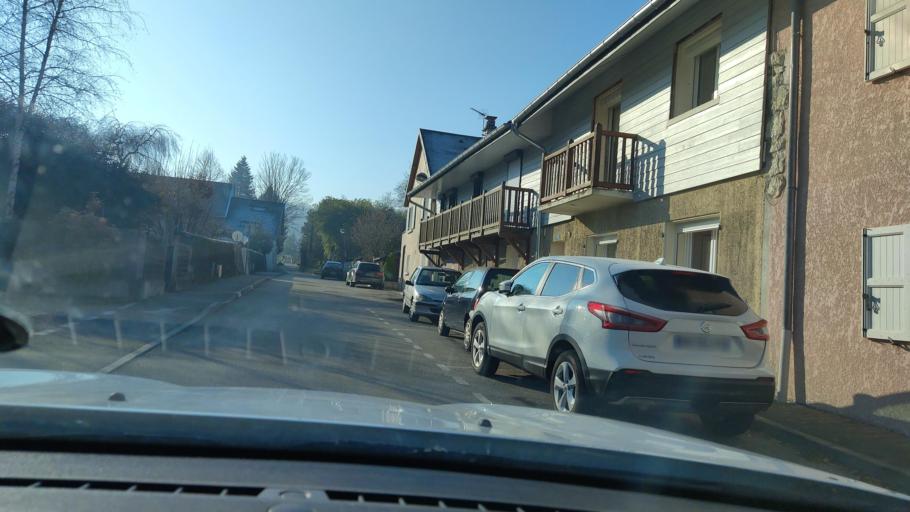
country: FR
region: Rhone-Alpes
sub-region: Departement de la Savoie
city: Viviers-du-Lac
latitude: 45.6473
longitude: 5.9048
